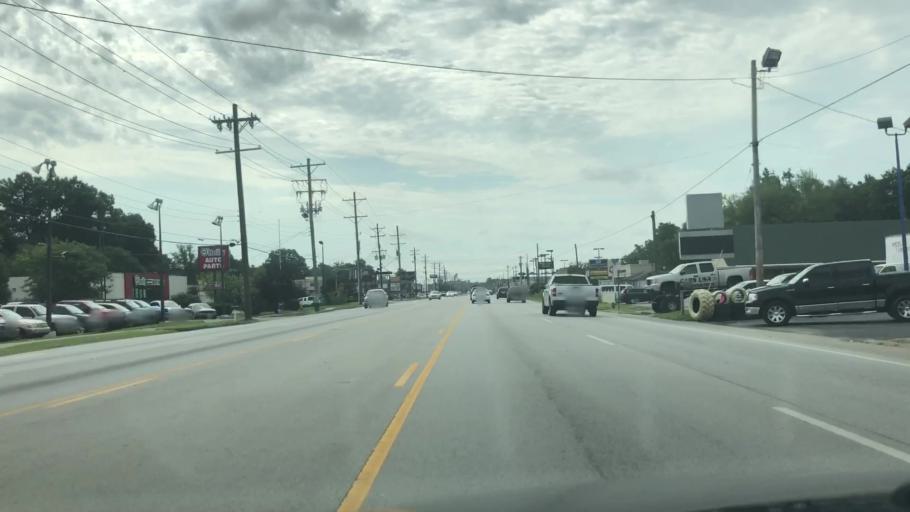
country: US
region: Kentucky
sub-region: Jefferson County
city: Audubon Park
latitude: 38.1741
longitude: -85.7122
